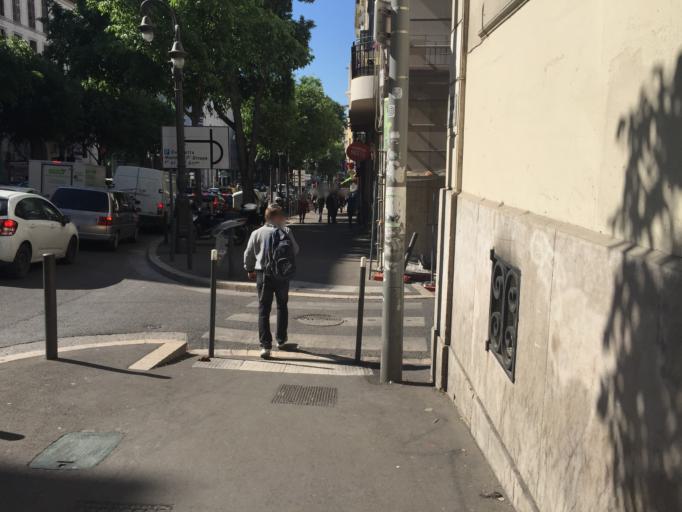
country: FR
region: Provence-Alpes-Cote d'Azur
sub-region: Departement des Bouches-du-Rhone
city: Marseille
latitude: 43.2999
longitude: 5.3809
